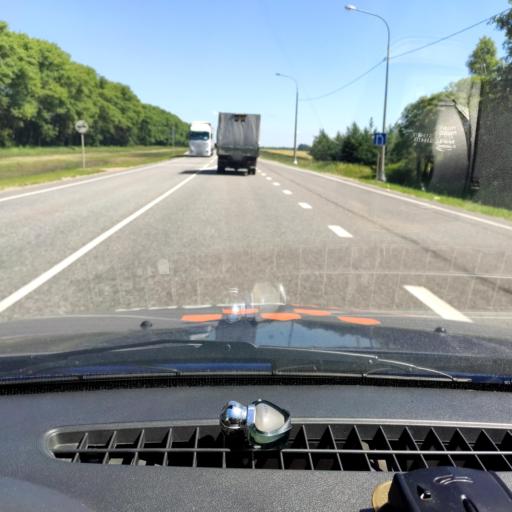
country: RU
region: Orjol
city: Pokrovskoye
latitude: 52.6407
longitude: 36.6731
